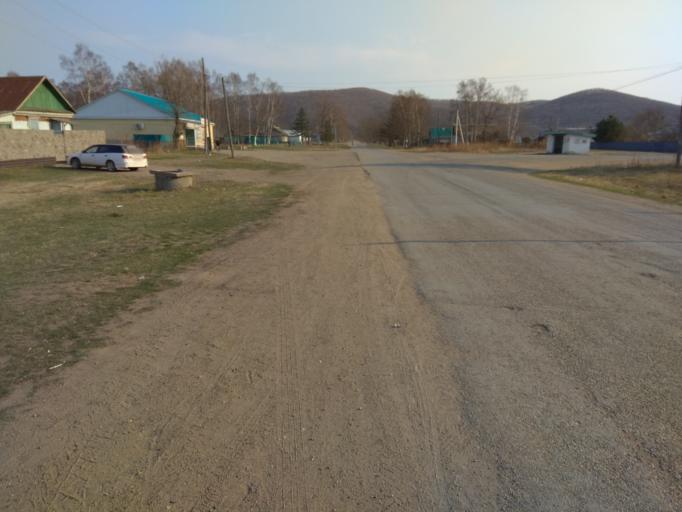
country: RU
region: Primorskiy
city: Lazo
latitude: 43.3081
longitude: 134.6040
